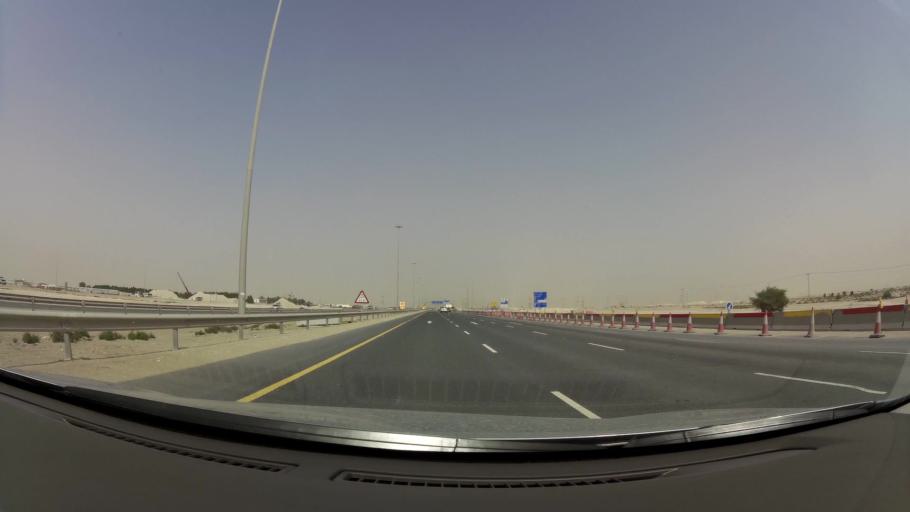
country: QA
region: Baladiyat ar Rayyan
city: Ar Rayyan
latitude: 25.1680
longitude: 51.3150
